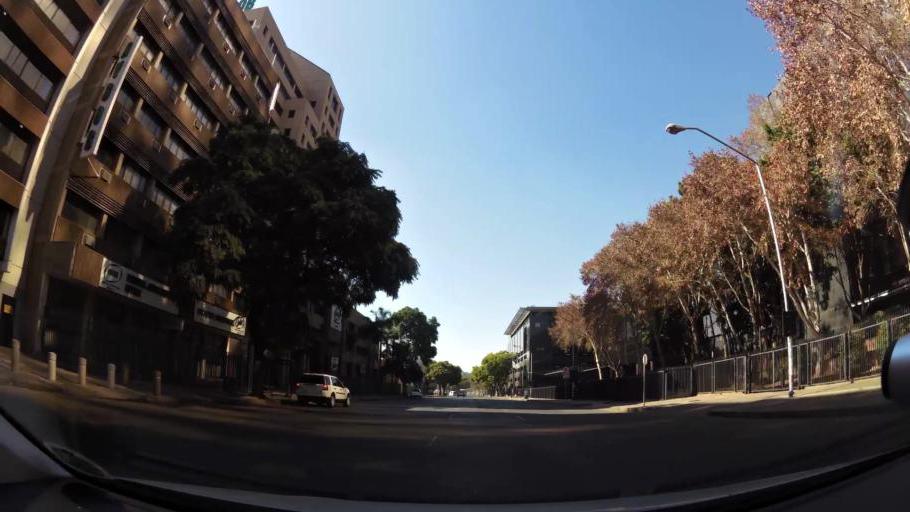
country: ZA
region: Gauteng
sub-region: City of Tshwane Metropolitan Municipality
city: Pretoria
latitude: -25.7444
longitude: 28.1957
